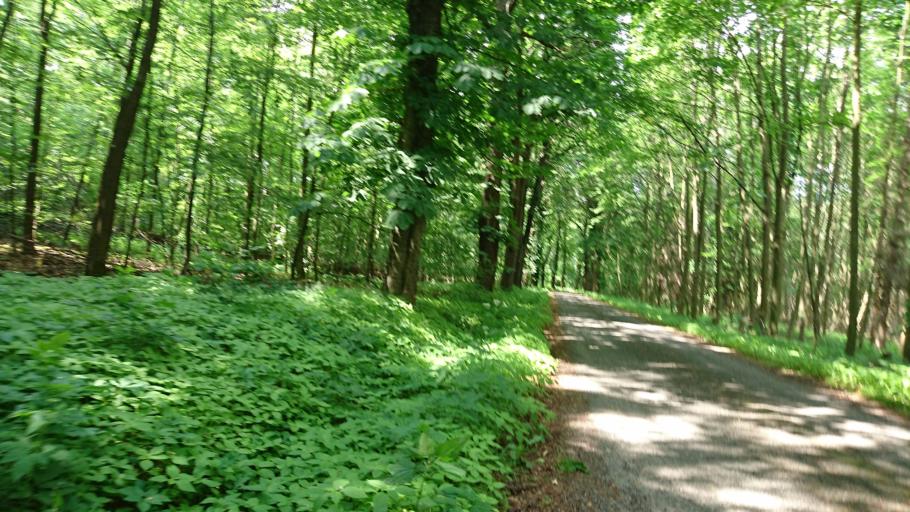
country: DE
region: Saxony
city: Bad Schandau
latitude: 50.8651
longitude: 14.1804
